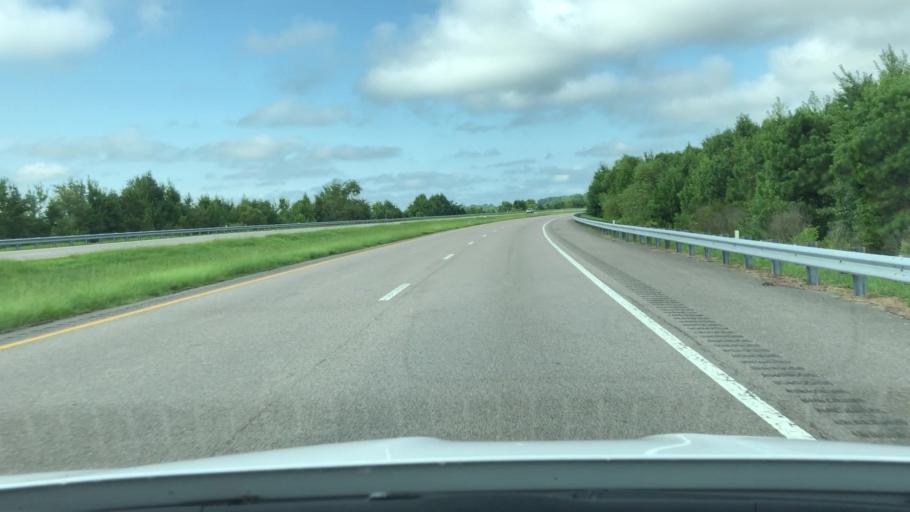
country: US
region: Virginia
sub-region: City of Portsmouth
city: Portsmouth Heights
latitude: 36.6190
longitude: -76.3680
